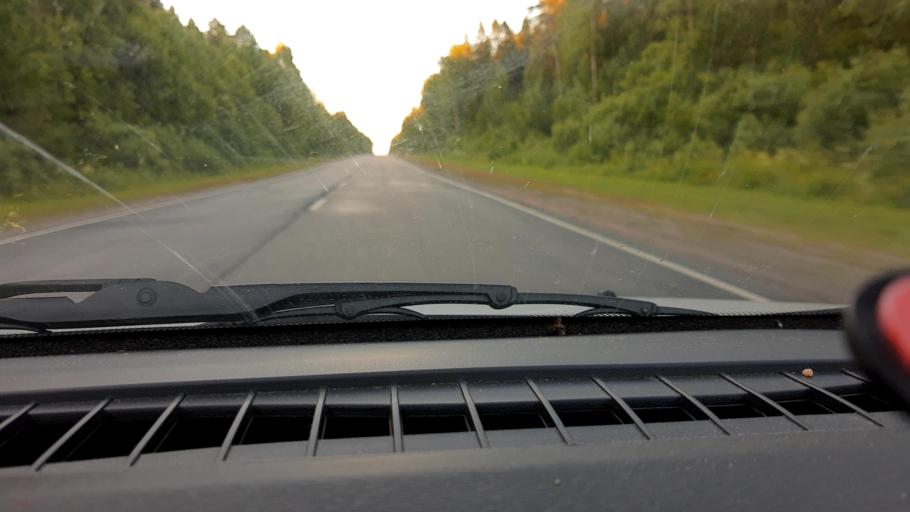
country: RU
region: Nizjnij Novgorod
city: Vladimirskoye
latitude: 56.9376
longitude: 45.0755
